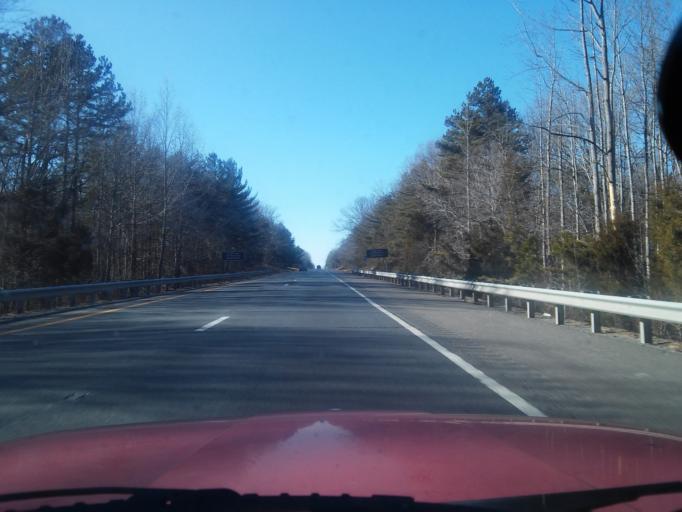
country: US
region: Virginia
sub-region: Fluvanna County
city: Lake Monticello
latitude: 37.9813
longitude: -78.2231
